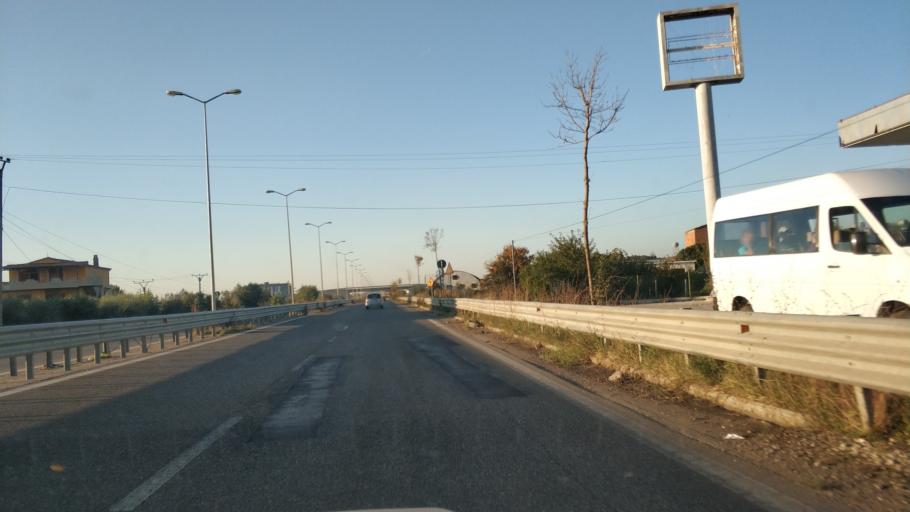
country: AL
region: Tirane
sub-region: Rrethi i Kavajes
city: Lekaj
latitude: 41.1113
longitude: 19.6063
